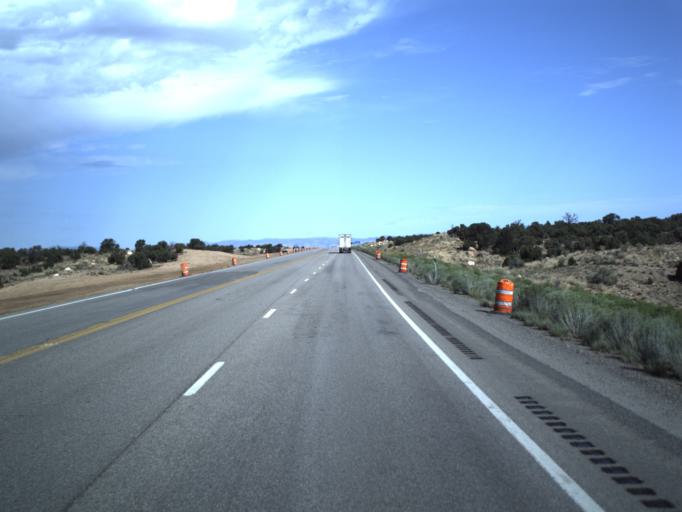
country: US
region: Utah
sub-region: Carbon County
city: East Carbon City
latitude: 39.4057
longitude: -110.4276
